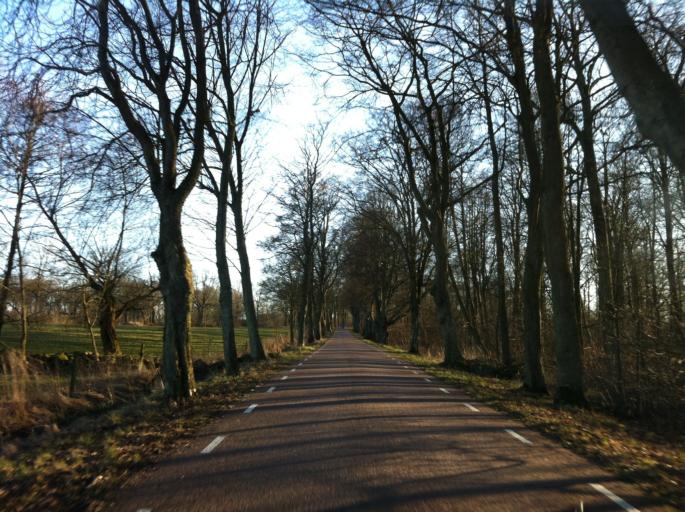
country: SE
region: Skane
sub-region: Helsingborg
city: Hyllinge
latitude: 56.0856
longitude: 12.8297
